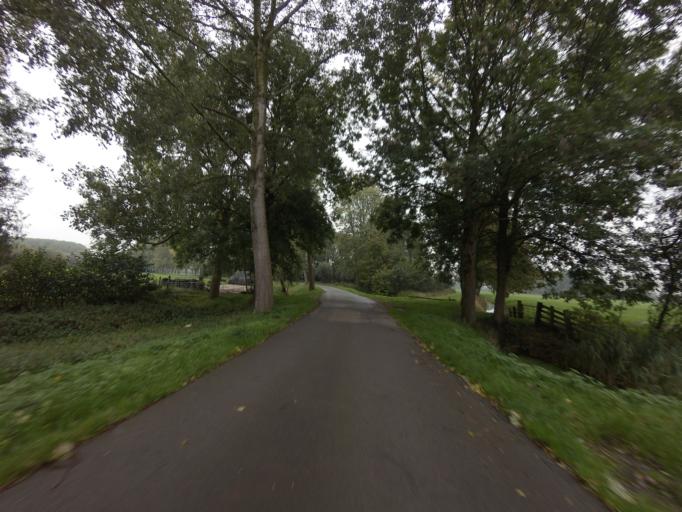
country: NL
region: South Holland
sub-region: Gemeente Leerdam
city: Leerdam
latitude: 51.9114
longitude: 5.1423
